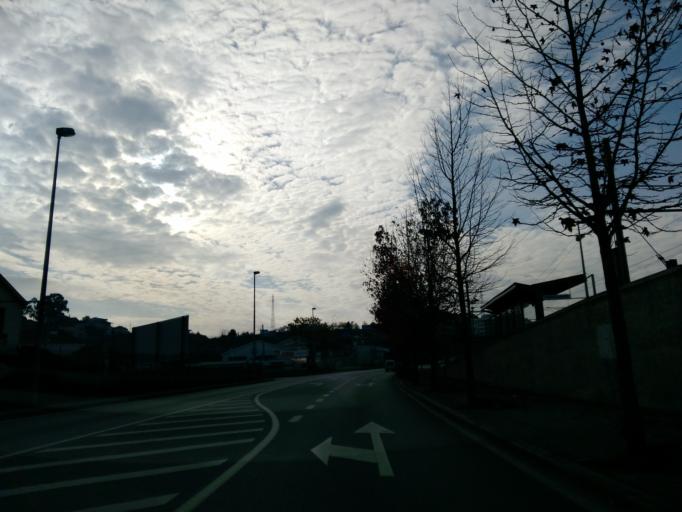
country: PT
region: Braga
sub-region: Braga
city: Braga
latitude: 41.5312
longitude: -8.4407
